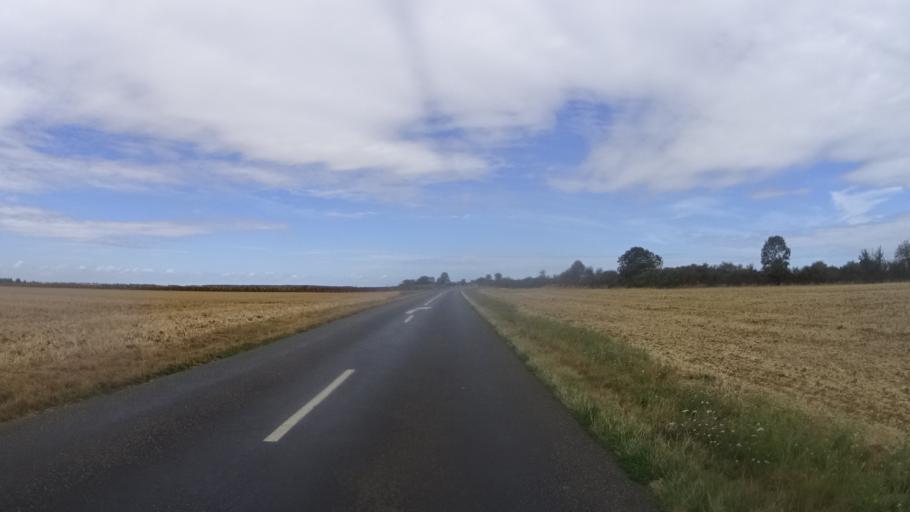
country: FR
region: Centre
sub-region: Departement du Loiret
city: Malesherbes
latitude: 48.2448
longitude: 2.4277
